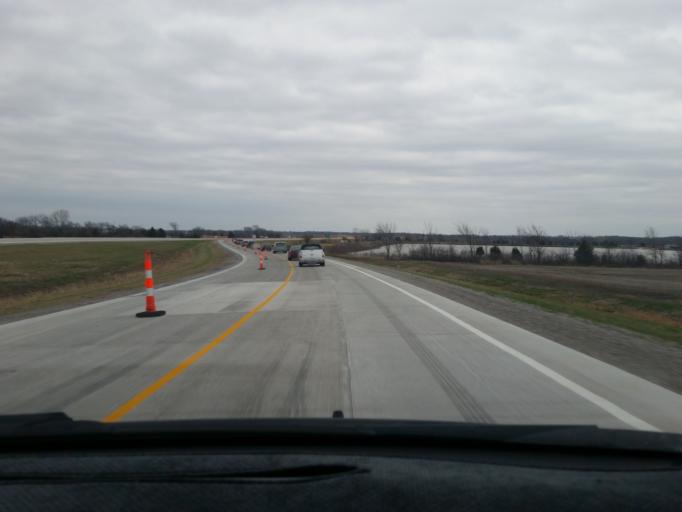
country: US
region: Kansas
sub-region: Douglas County
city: Eudora
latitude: 38.9344
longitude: -95.1686
